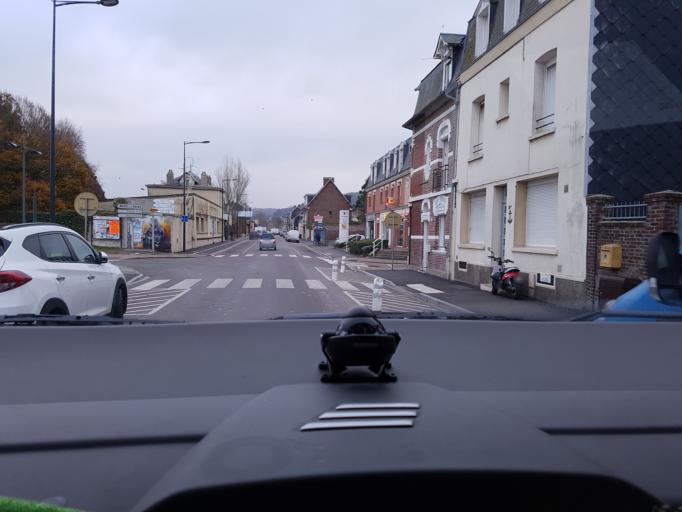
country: FR
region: Haute-Normandie
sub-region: Departement de la Seine-Maritime
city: Le Treport
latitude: 50.0593
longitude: 1.3807
